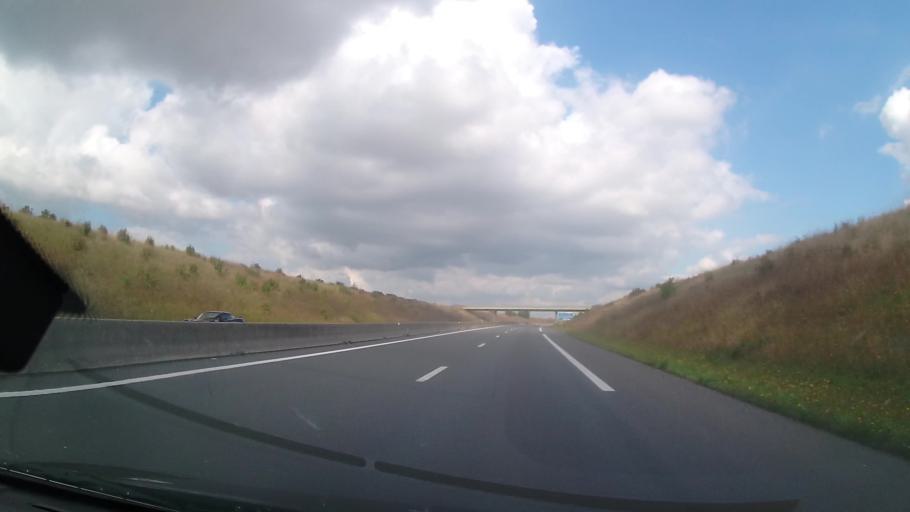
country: FR
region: Nord-Pas-de-Calais
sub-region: Departement du Pas-de-Calais
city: Verton
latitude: 50.3558
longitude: 1.6882
